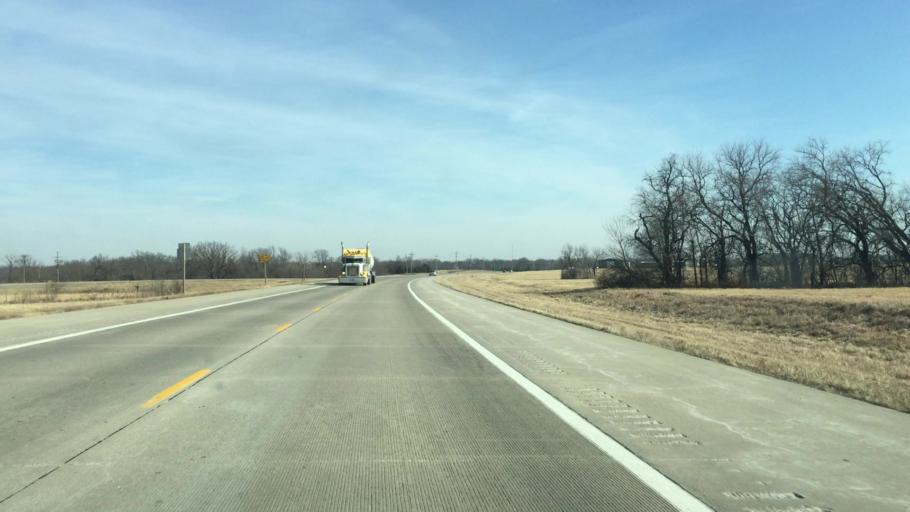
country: US
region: Kansas
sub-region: Labette County
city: Parsons
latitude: 37.3674
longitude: -95.2952
